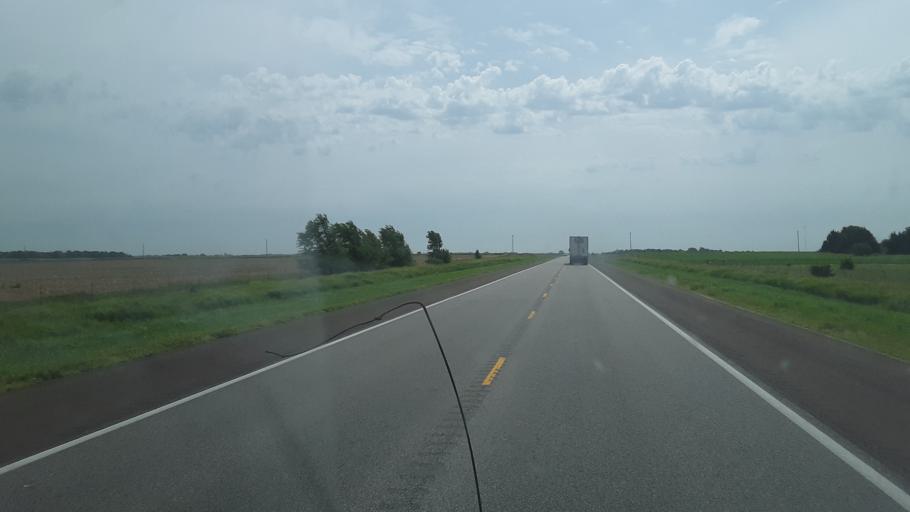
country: US
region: Kansas
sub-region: Reno County
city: Nickerson
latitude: 37.9849
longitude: -98.1104
